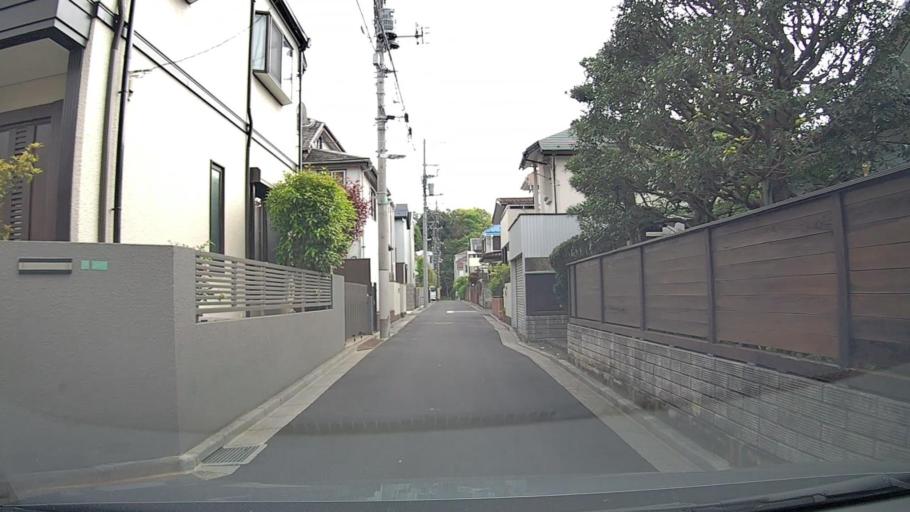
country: JP
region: Tokyo
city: Musashino
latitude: 35.7296
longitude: 139.5859
